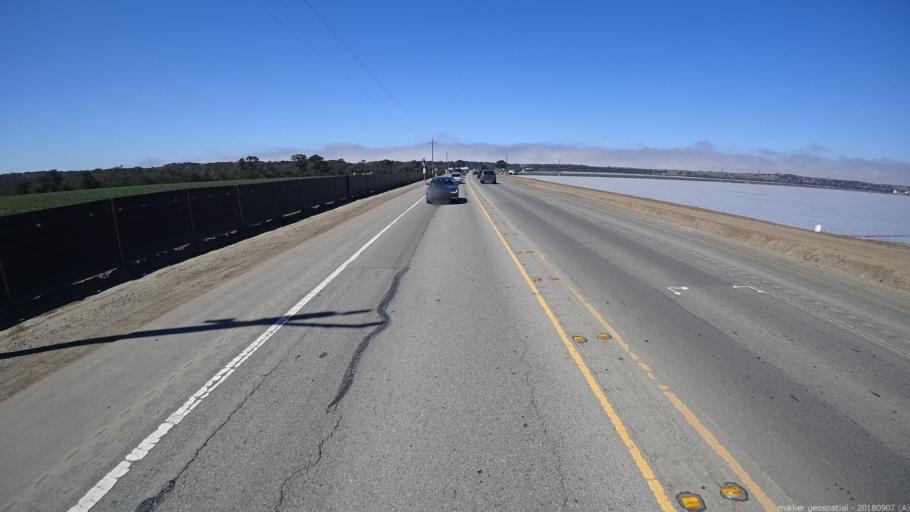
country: US
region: California
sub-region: Monterey County
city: Marina
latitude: 36.6787
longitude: -121.7373
